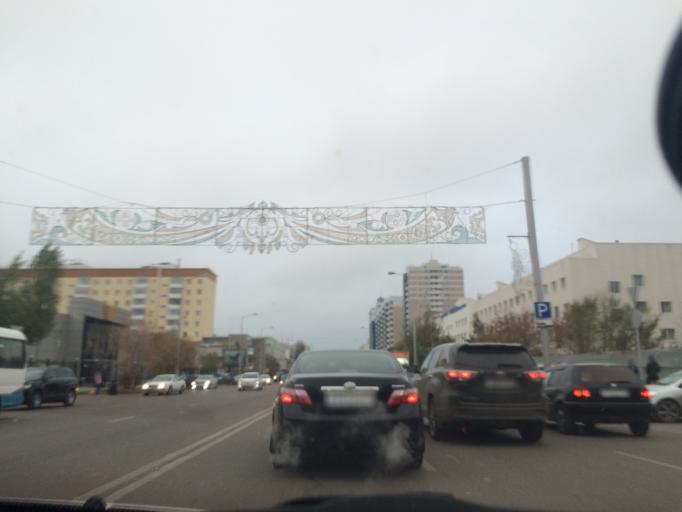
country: KZ
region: Astana Qalasy
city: Astana
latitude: 51.1712
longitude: 71.4074
